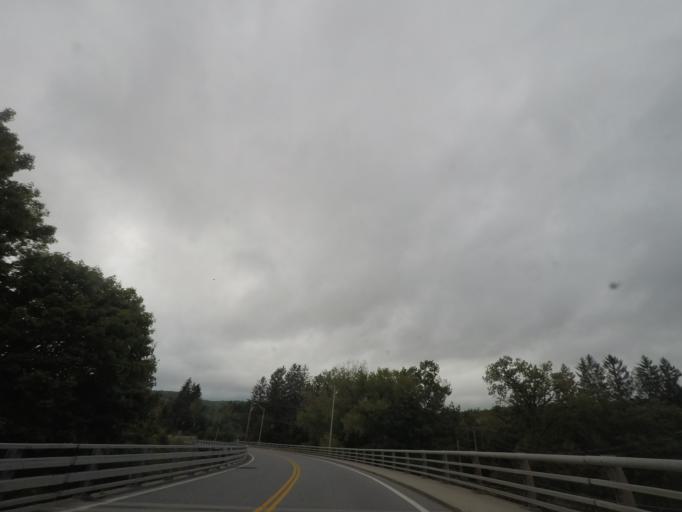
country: US
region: New York
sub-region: Rensselaer County
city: Hoosick Falls
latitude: 42.8960
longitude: -73.3591
